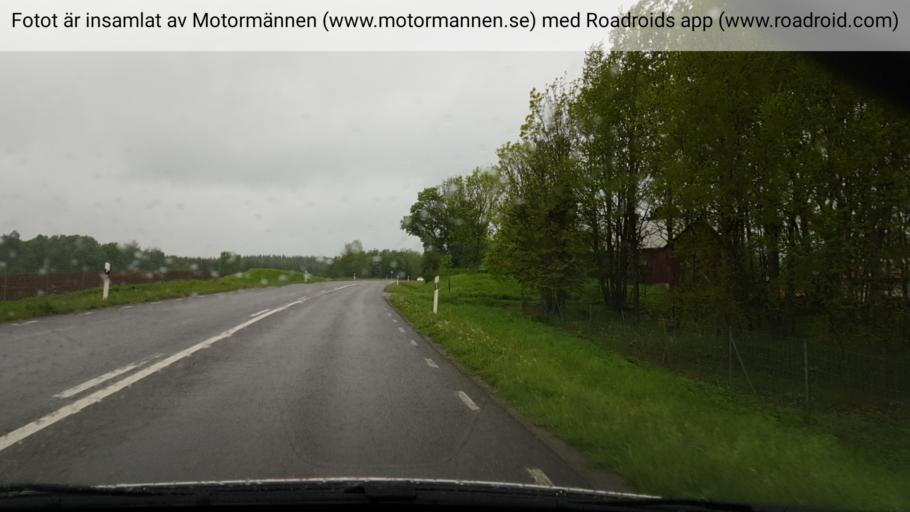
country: SE
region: Vaestra Goetaland
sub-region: Falkopings Kommun
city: Falkoeping
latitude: 58.0644
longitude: 13.5316
